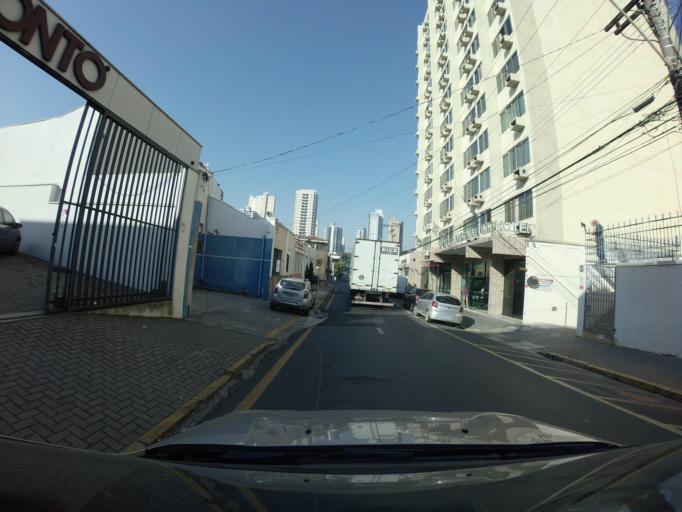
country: BR
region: Sao Paulo
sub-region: Piracicaba
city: Piracicaba
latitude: -22.7274
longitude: -47.6531
